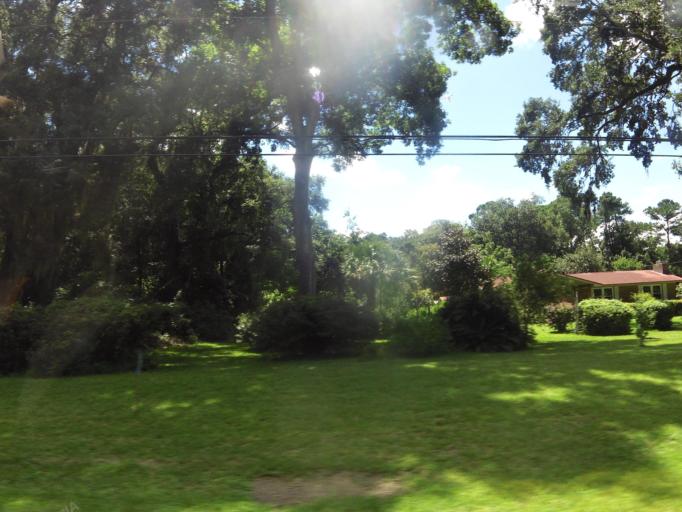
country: US
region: Florida
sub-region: Nassau County
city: Yulee
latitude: 30.6318
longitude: -81.5296
